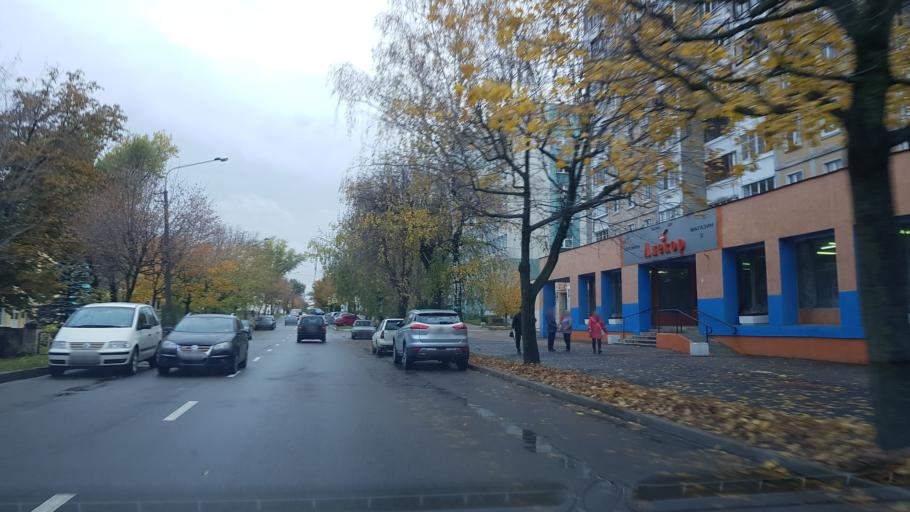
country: BY
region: Minsk
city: Syenitsa
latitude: 53.8487
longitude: 27.5511
